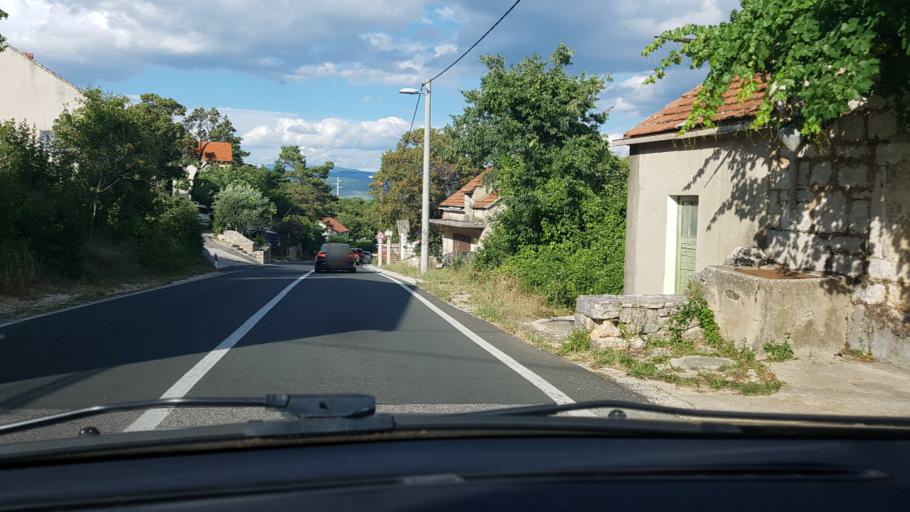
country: HR
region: Splitsko-Dalmatinska
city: Grubine
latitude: 43.4213
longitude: 17.1157
